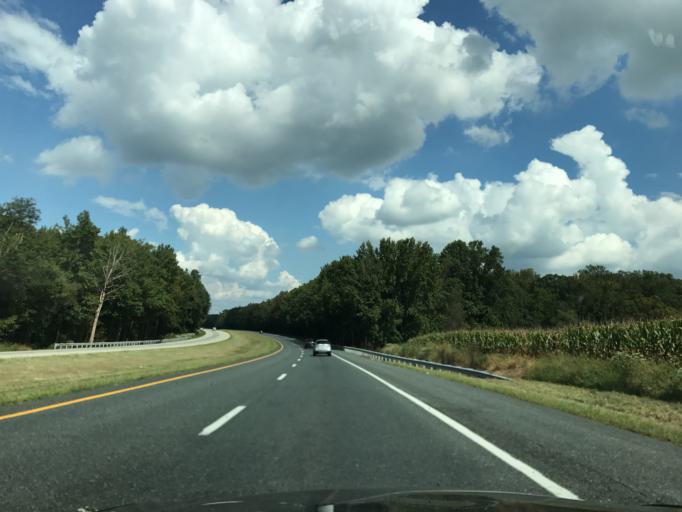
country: US
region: Maryland
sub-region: Queen Anne's County
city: Kingstown
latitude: 39.2038
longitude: -75.8924
